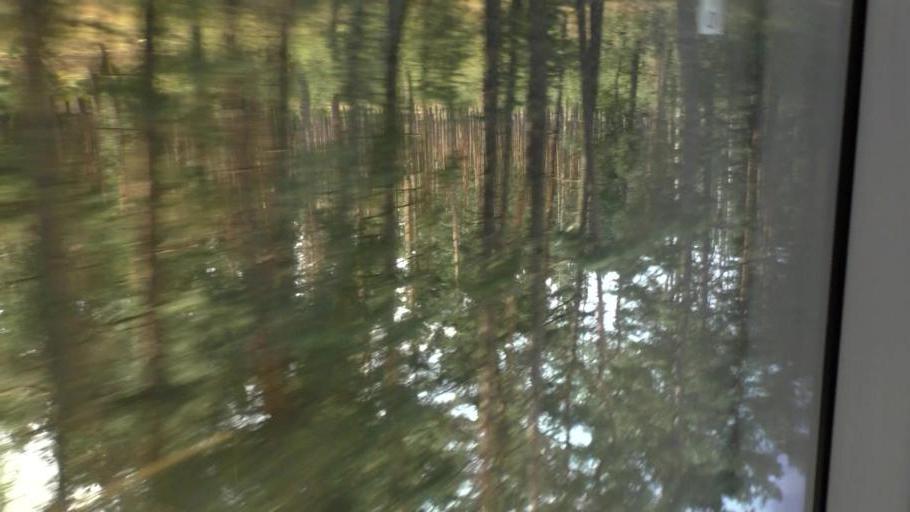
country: DE
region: Brandenburg
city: Mixdorf
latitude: 52.1619
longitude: 14.3698
